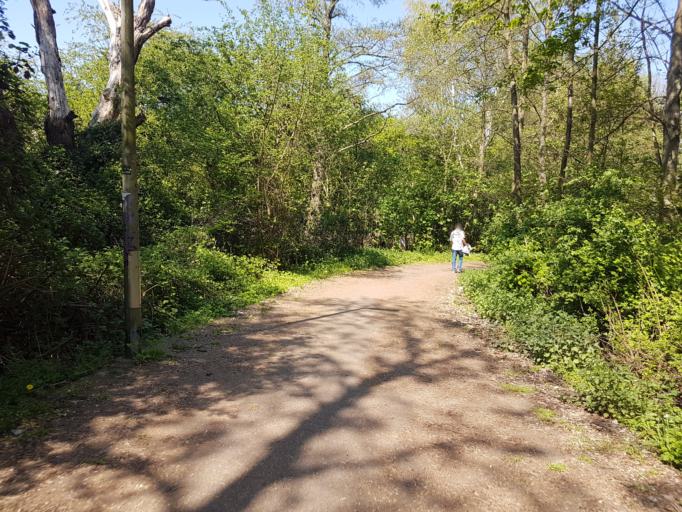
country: DE
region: North Rhine-Westphalia
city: Witten
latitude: 51.4331
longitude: 7.3158
